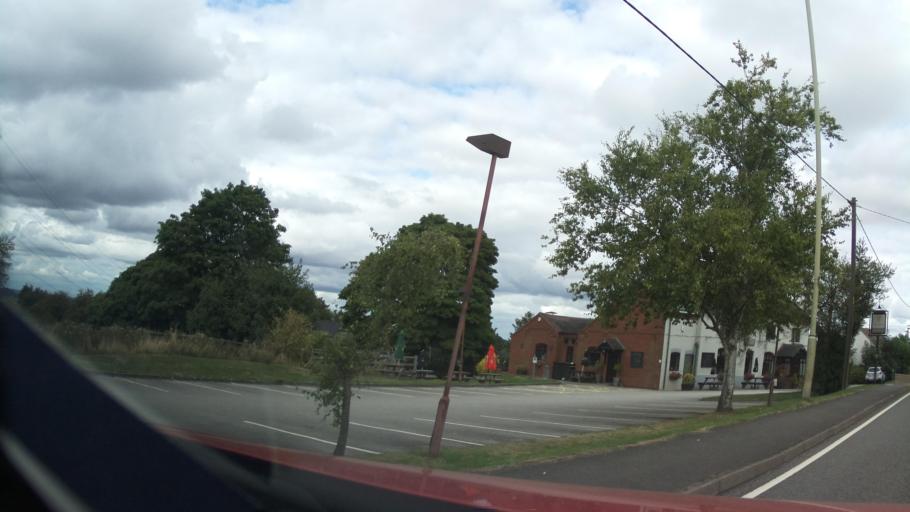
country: GB
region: England
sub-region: Leicestershire
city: Coalville
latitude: 52.7516
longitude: -1.3996
